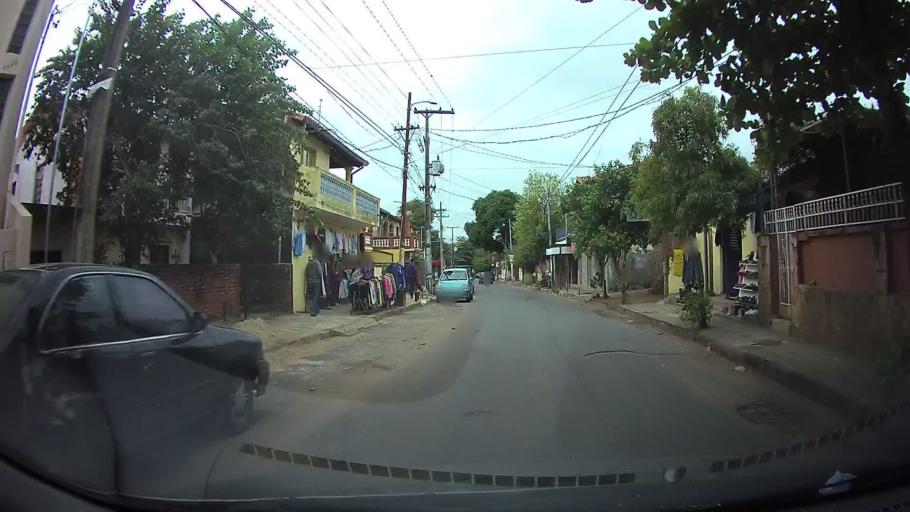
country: PY
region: Central
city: Lambare
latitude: -25.3199
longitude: -57.6084
